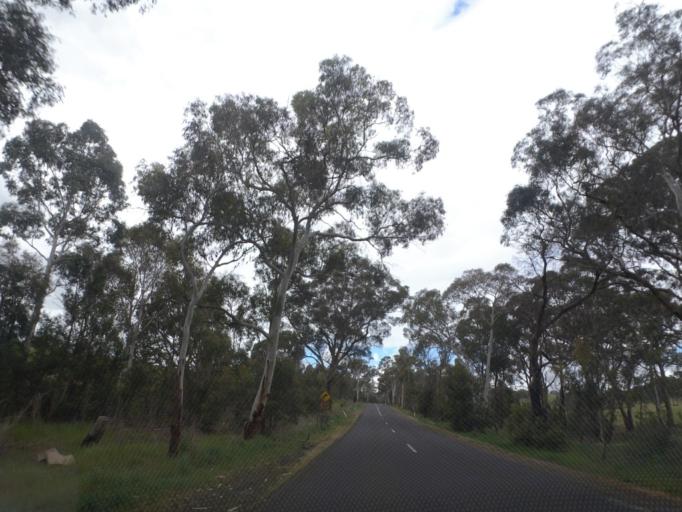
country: AU
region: Victoria
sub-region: Hume
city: Craigieburn
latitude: -37.3953
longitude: 144.9310
